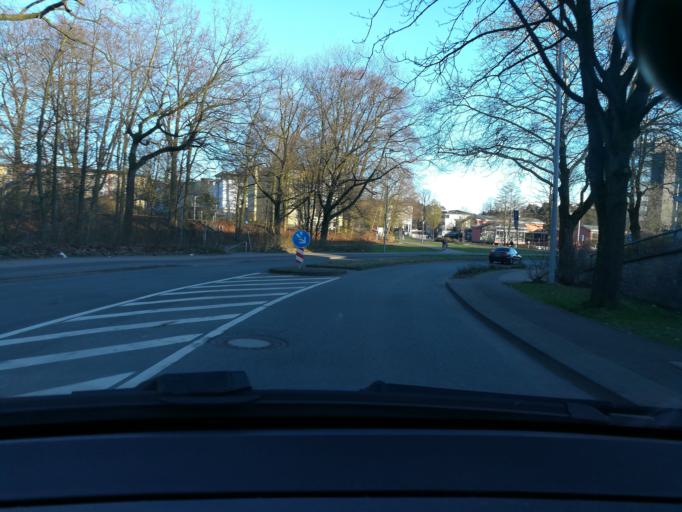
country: DE
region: North Rhine-Westphalia
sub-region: Regierungsbezirk Detmold
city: Oerlinghausen
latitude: 51.9473
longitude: 8.5830
